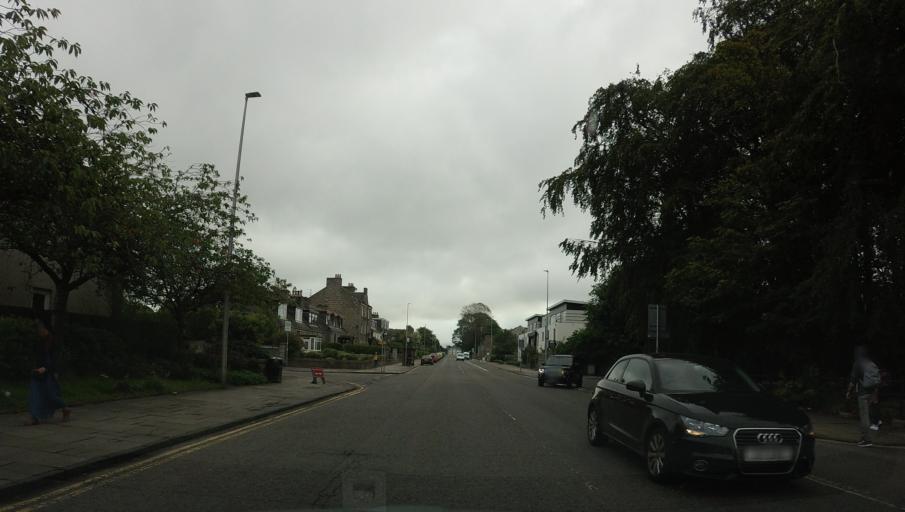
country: GB
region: Scotland
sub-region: Aberdeen City
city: Aberdeen
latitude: 57.1260
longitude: -2.1200
